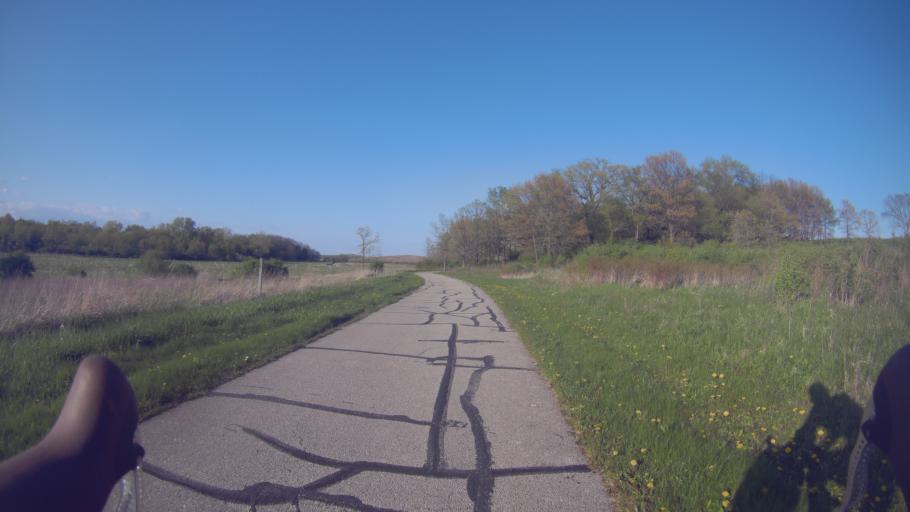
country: US
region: Wisconsin
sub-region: Dane County
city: Monona
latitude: 43.0235
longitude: -89.3541
